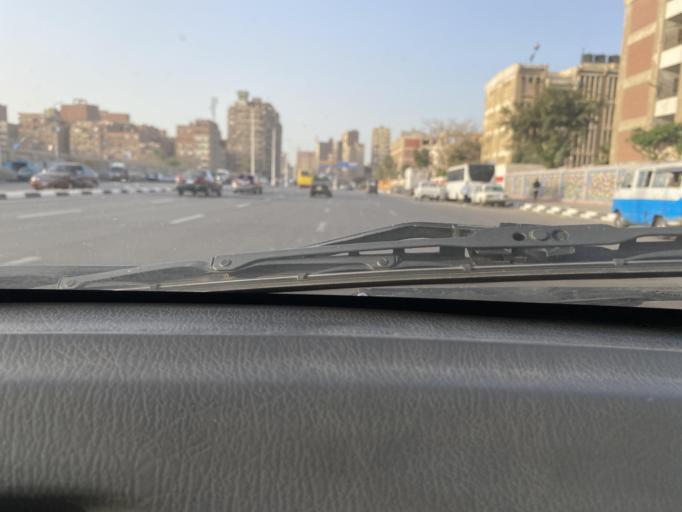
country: EG
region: Muhafazat al Qahirah
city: Cairo
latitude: 30.1160
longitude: 31.2964
